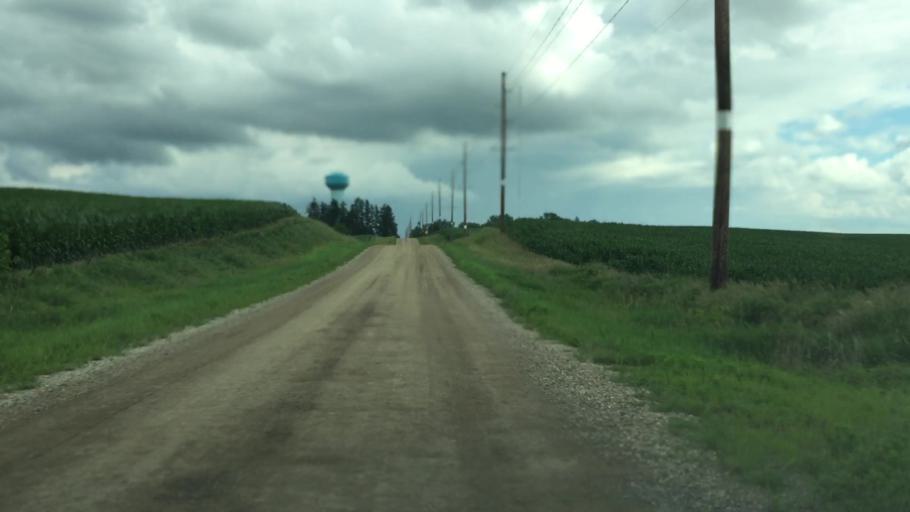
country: US
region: Iowa
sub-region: Jasper County
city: Newton
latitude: 41.7409
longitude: -93.0195
